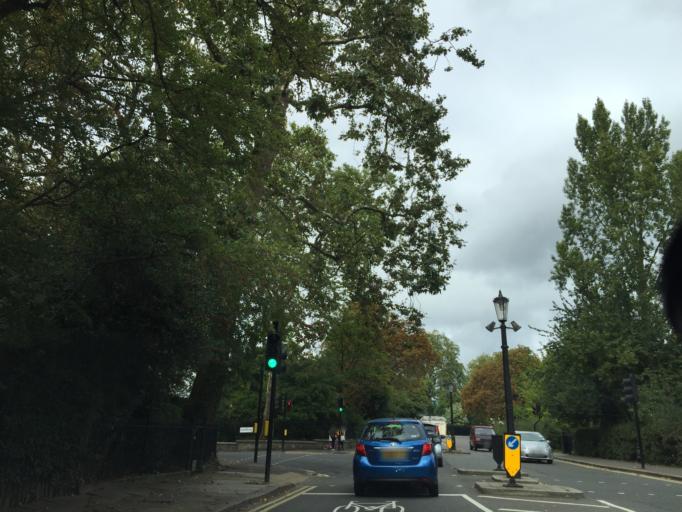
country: GB
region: England
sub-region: Greater London
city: Belsize Park
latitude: 51.5286
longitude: -0.1634
